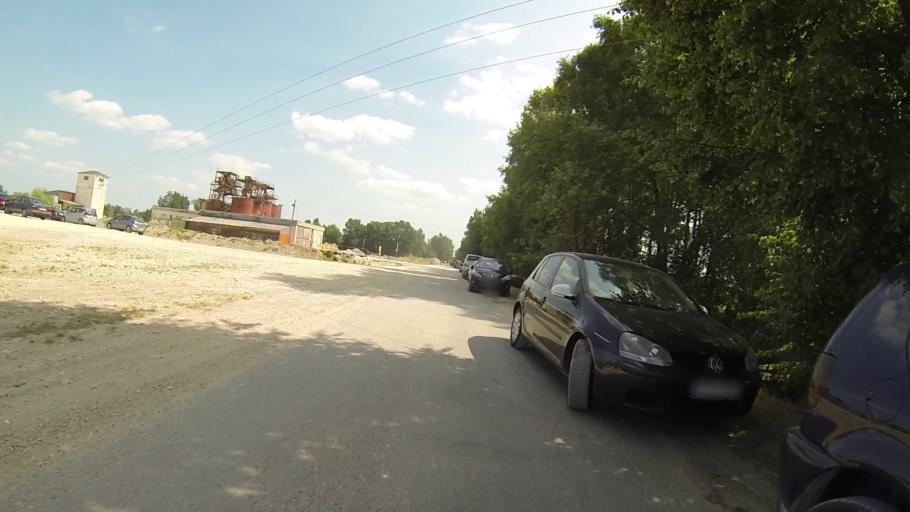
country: DE
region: Bavaria
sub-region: Swabia
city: Guenzburg
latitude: 48.5028
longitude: 10.2650
